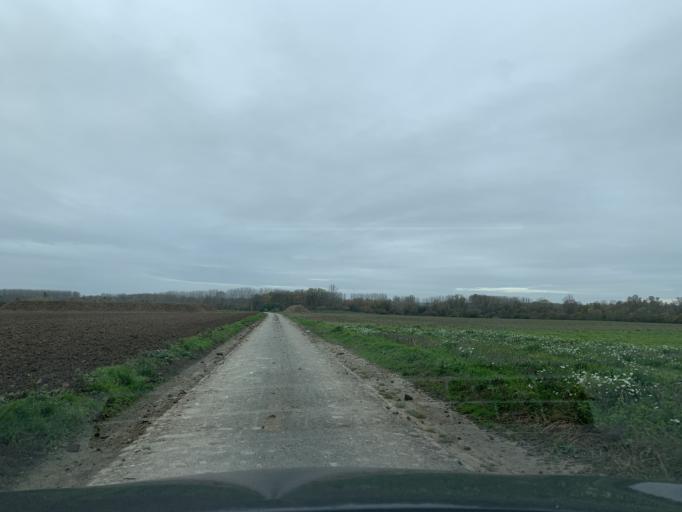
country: FR
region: Nord-Pas-de-Calais
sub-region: Departement du Pas-de-Calais
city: Oisy-le-Verger
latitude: 50.2513
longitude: 3.1058
